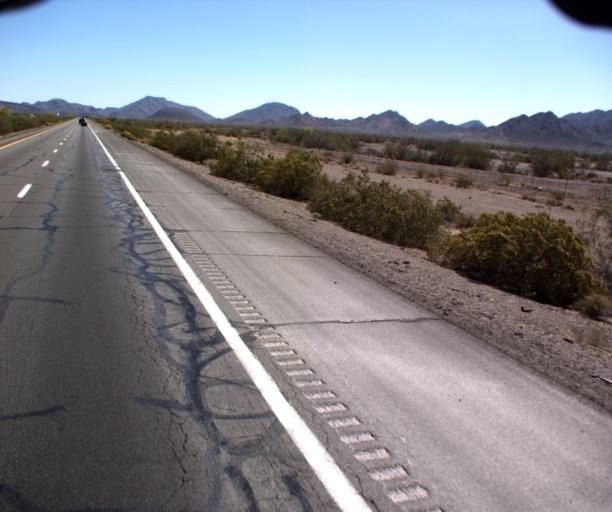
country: US
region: Arizona
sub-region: La Paz County
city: Quartzsite
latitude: 33.6738
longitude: -114.1377
